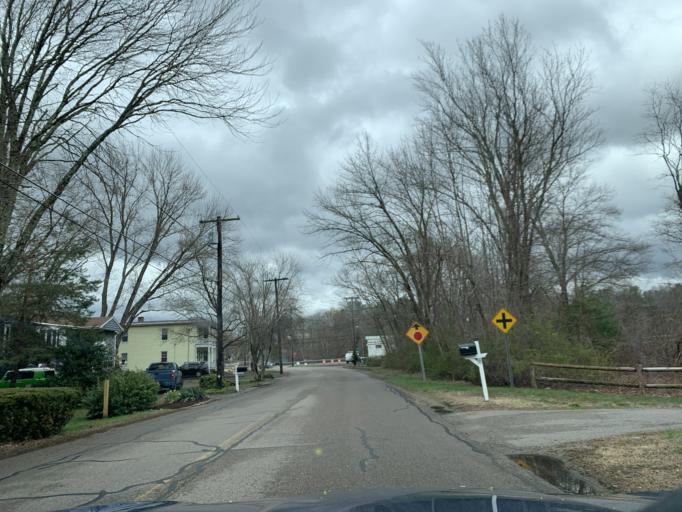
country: US
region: Massachusetts
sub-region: Bristol County
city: Norton
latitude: 41.9512
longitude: -71.2292
